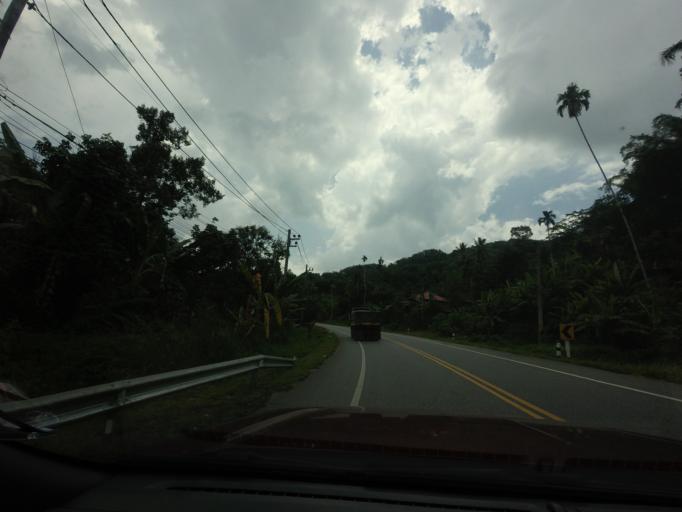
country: TH
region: Yala
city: Than To
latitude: 6.0799
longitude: 101.1865
